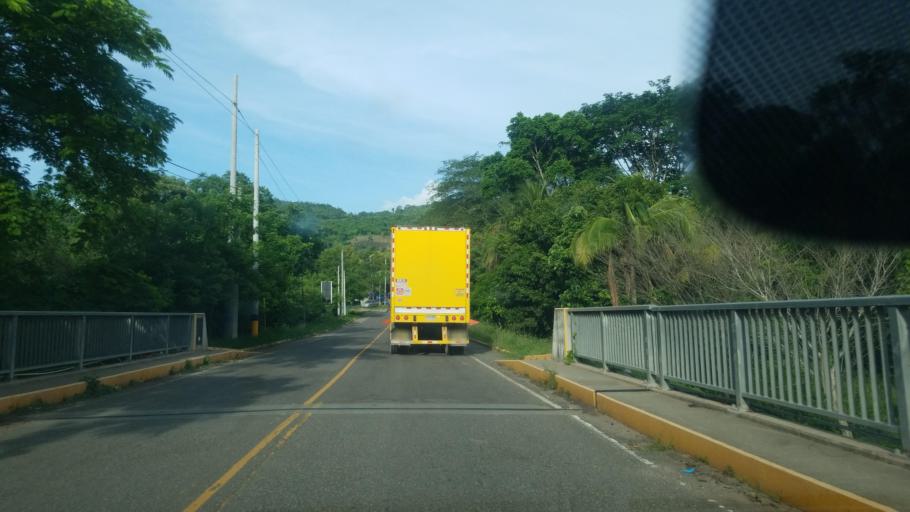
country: HN
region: Santa Barbara
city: Ilama
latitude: 15.0663
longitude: -88.2279
